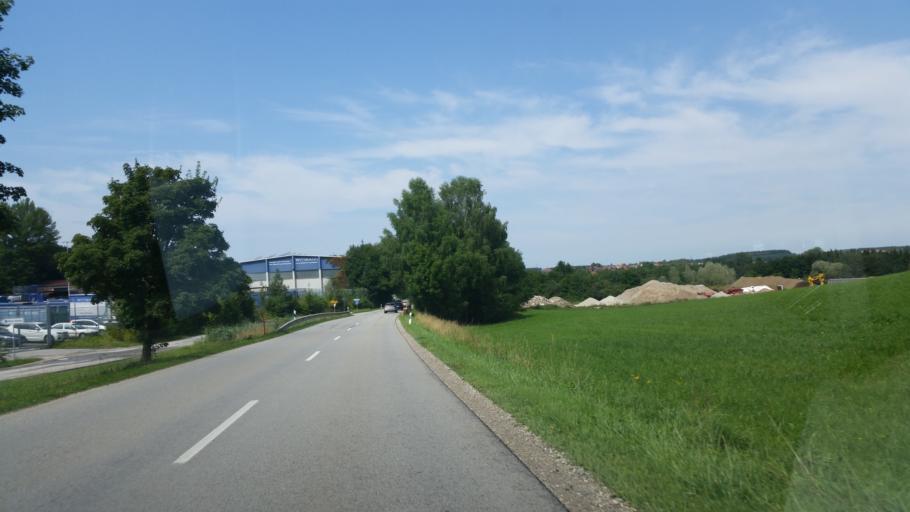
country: DE
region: Bavaria
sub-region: Lower Bavaria
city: Geisenhausen
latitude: 48.4726
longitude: 12.2728
